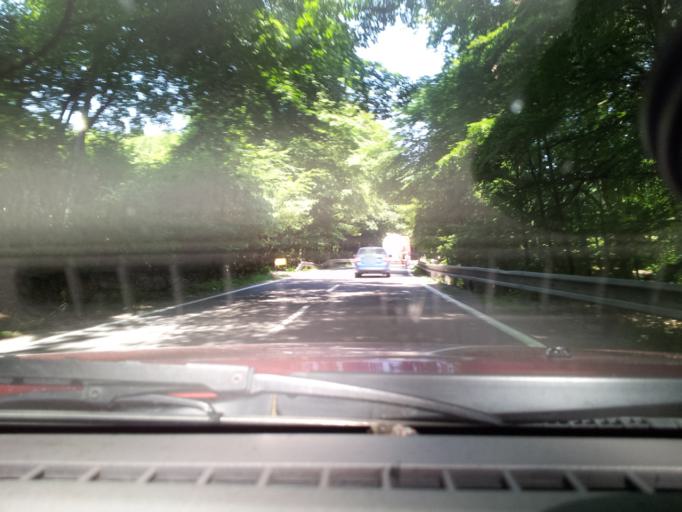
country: SK
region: Trnavsky
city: Smolenice
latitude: 48.5712
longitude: 17.4632
